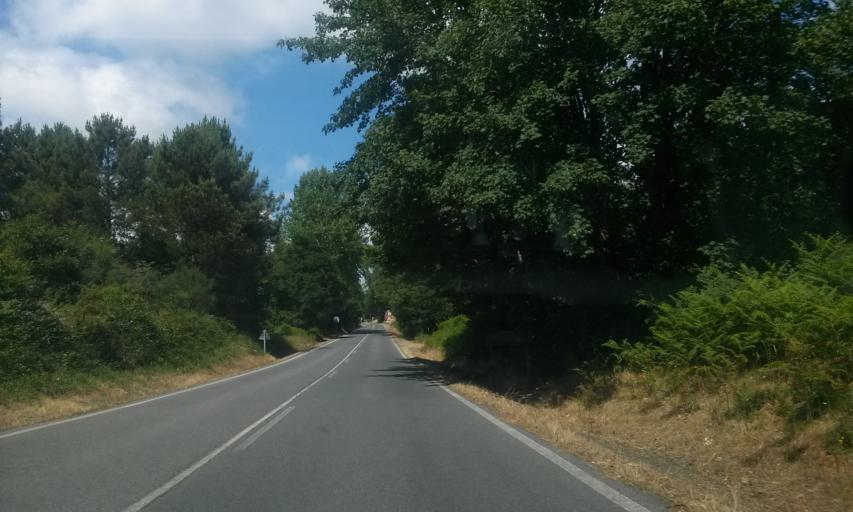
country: ES
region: Galicia
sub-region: Provincia de Lugo
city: Guitiriz
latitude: 43.1753
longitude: -7.8321
